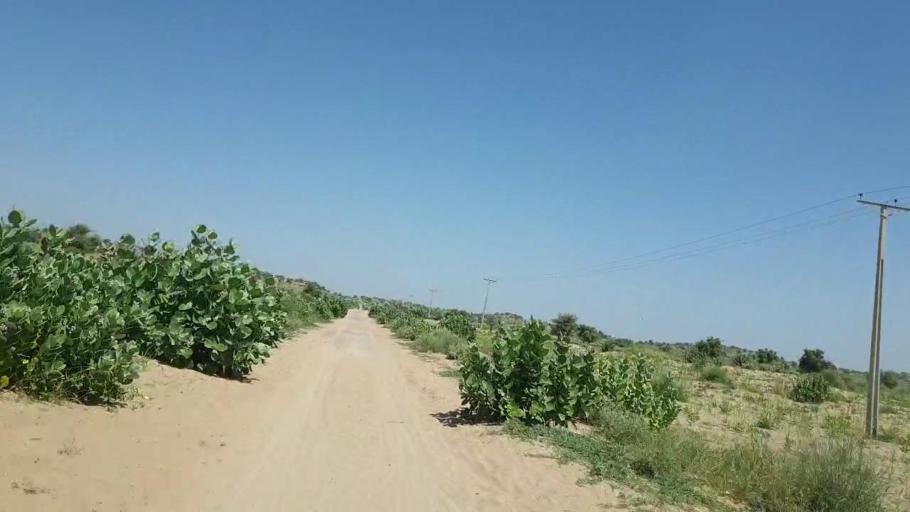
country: PK
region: Sindh
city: Islamkot
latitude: 25.1658
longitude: 70.4151
